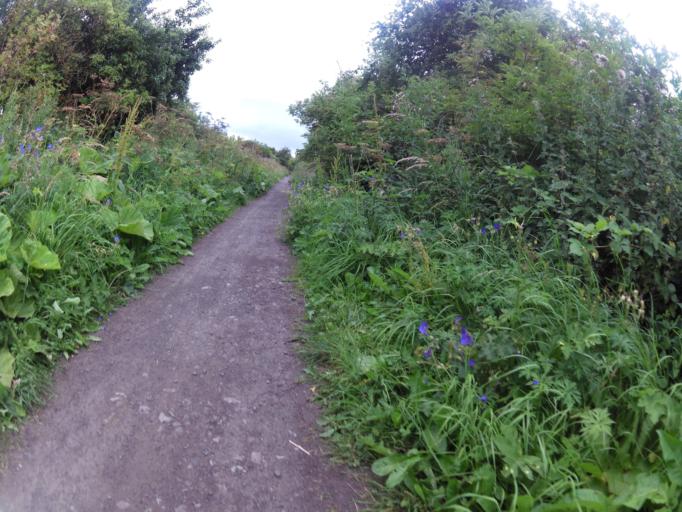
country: GB
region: Scotland
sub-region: Edinburgh
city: Kirkliston
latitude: 55.9518
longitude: -3.4008
